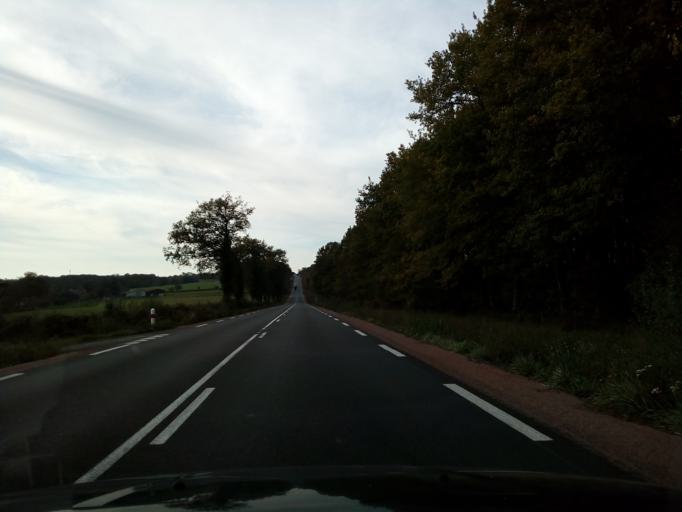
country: FR
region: Limousin
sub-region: Departement de la Haute-Vienne
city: Chateauponsac
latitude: 46.1916
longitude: 1.2524
